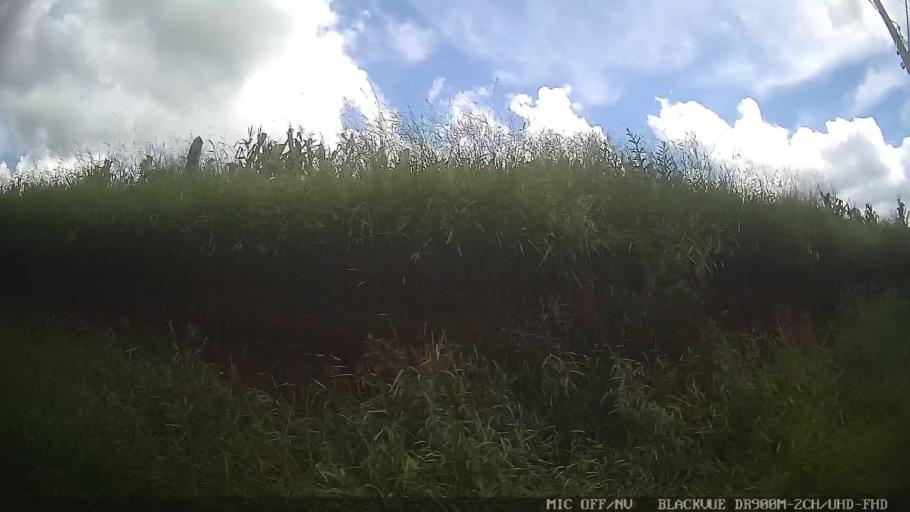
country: BR
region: Minas Gerais
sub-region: Extrema
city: Extrema
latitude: -22.8475
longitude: -46.2735
